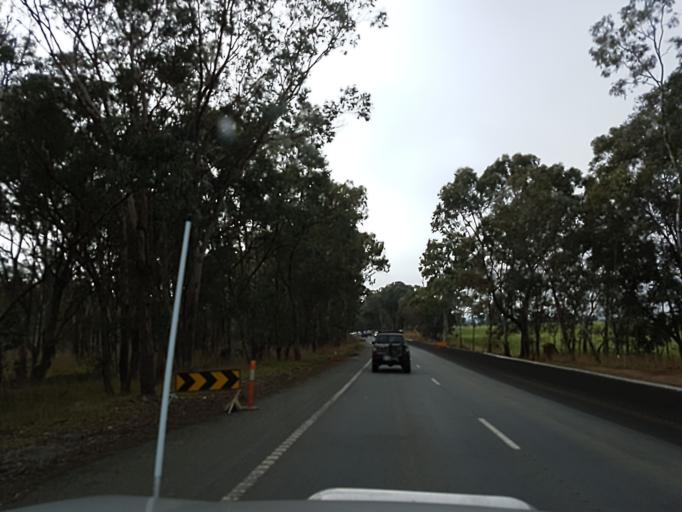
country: AU
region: Victoria
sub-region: Murrindindi
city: Alexandra
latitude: -37.1775
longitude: 145.4968
